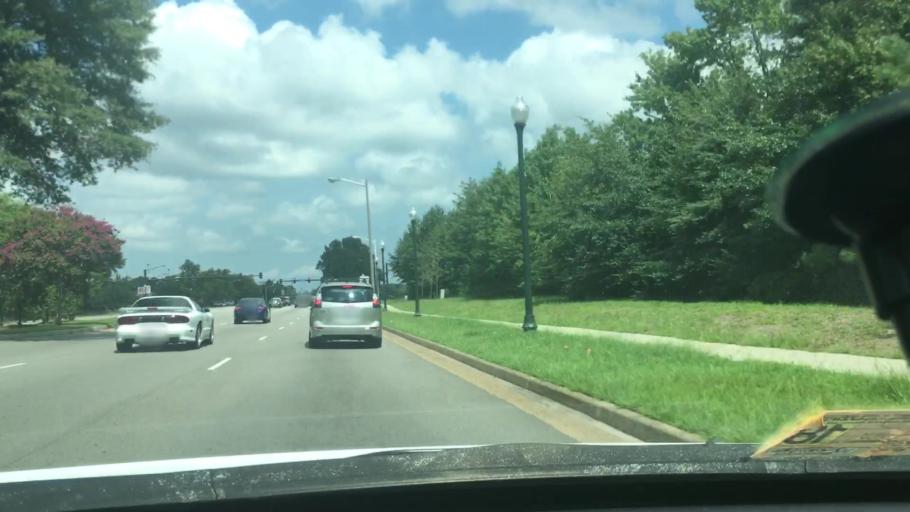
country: US
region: Virginia
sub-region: City of Chesapeake
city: Chesapeake
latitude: 36.7731
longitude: -76.2290
